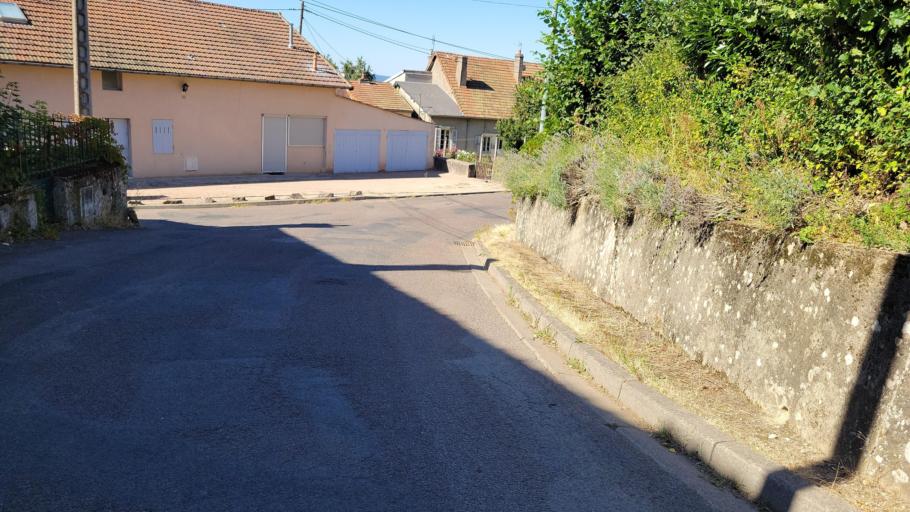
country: FR
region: Bourgogne
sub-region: Departement de Saone-et-Loire
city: Autun
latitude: 46.9414
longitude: 4.3128
